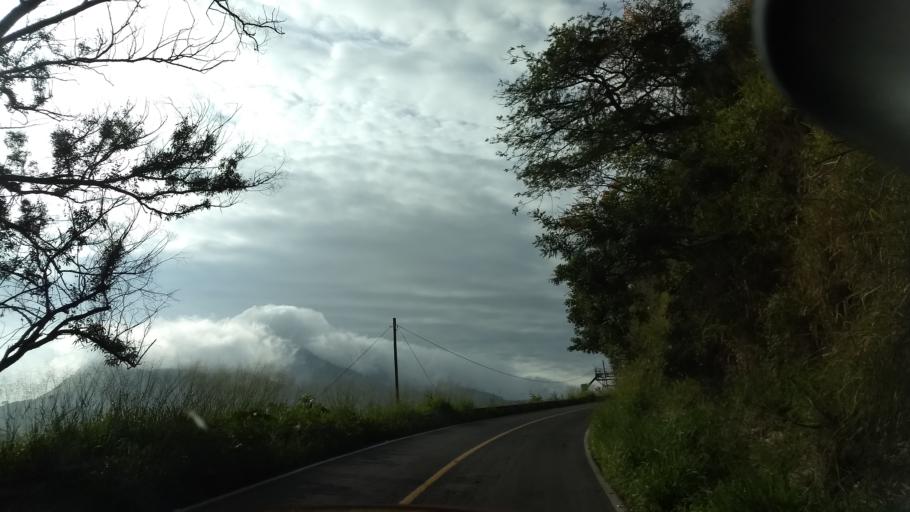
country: MX
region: Jalisco
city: Tuxpan
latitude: 19.5263
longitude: -103.4405
